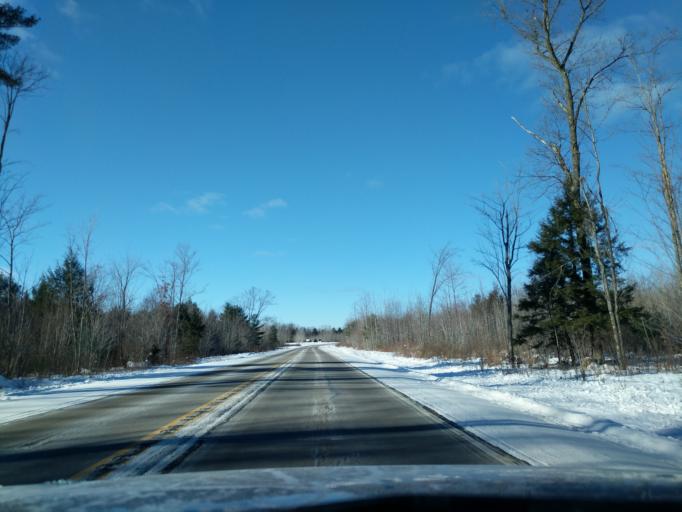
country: US
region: Wisconsin
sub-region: Menominee County
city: Keshena
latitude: 45.1497
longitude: -88.6887
